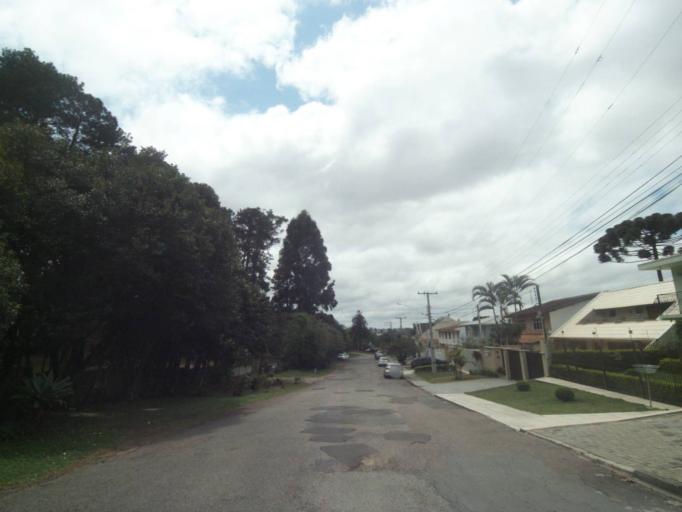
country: BR
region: Parana
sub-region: Pinhais
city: Pinhais
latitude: -25.4092
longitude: -49.2260
